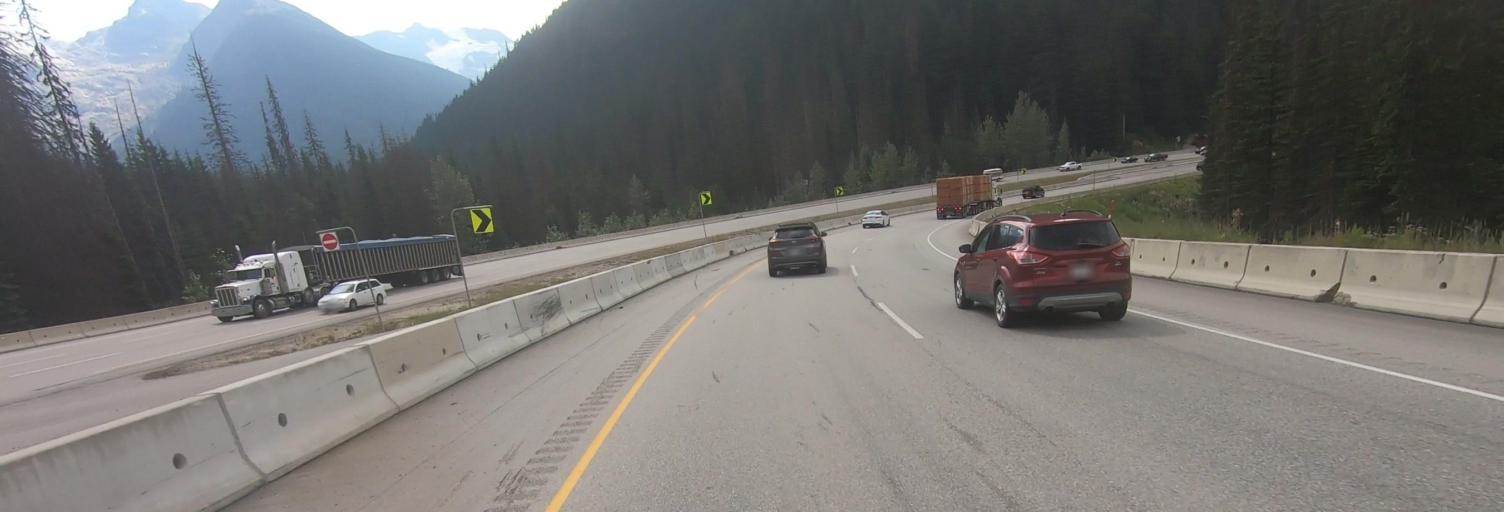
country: CA
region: British Columbia
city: Golden
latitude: 51.2706
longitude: -117.5037
